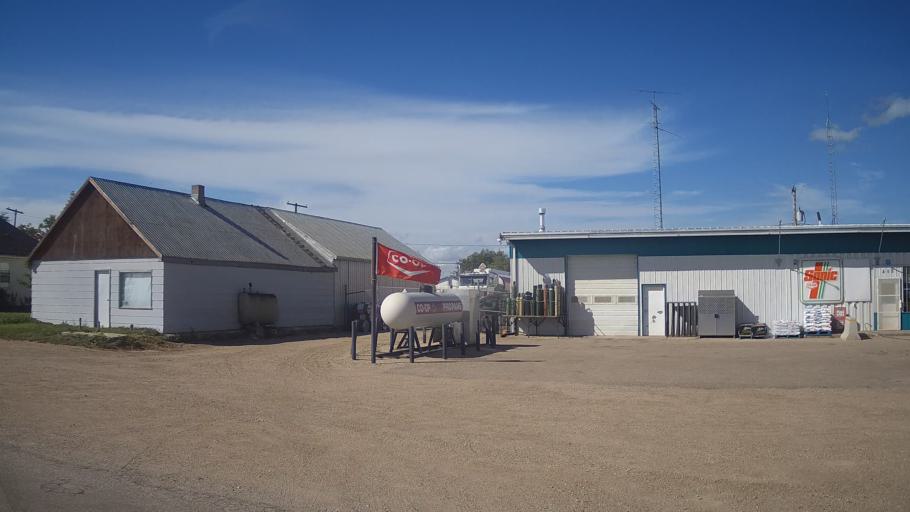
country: CA
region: Saskatchewan
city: Foam Lake
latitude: 51.2621
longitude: -103.7369
